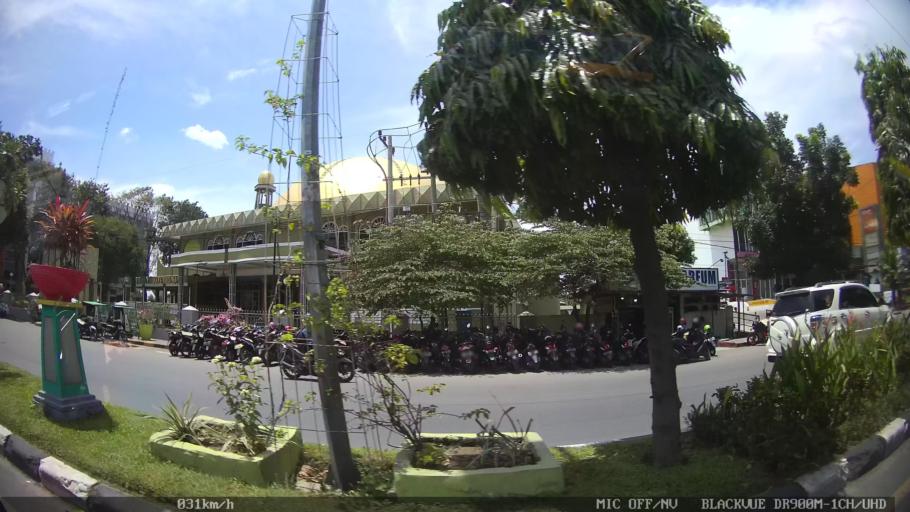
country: ID
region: North Sumatra
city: Binjai
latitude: 3.6084
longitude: 98.4964
